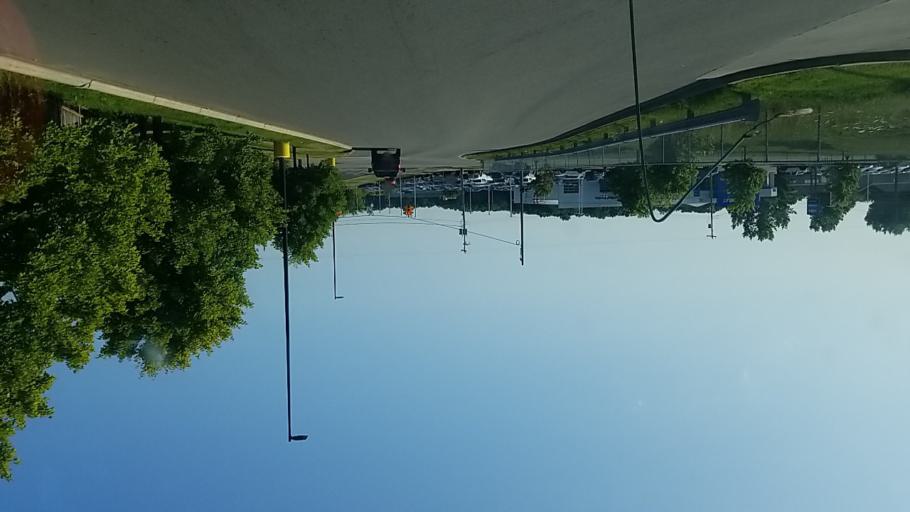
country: US
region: Michigan
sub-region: Newaygo County
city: Fremont
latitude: 43.4680
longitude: -85.9771
